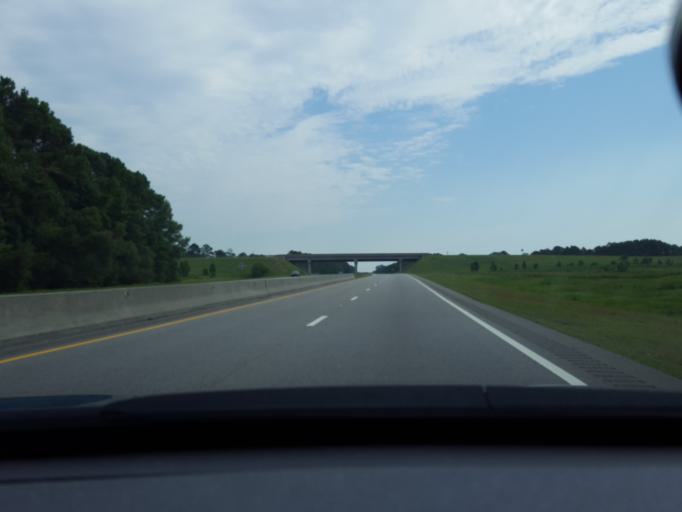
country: US
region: North Carolina
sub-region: Chowan County
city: Edenton
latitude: 36.0586
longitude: -76.6715
